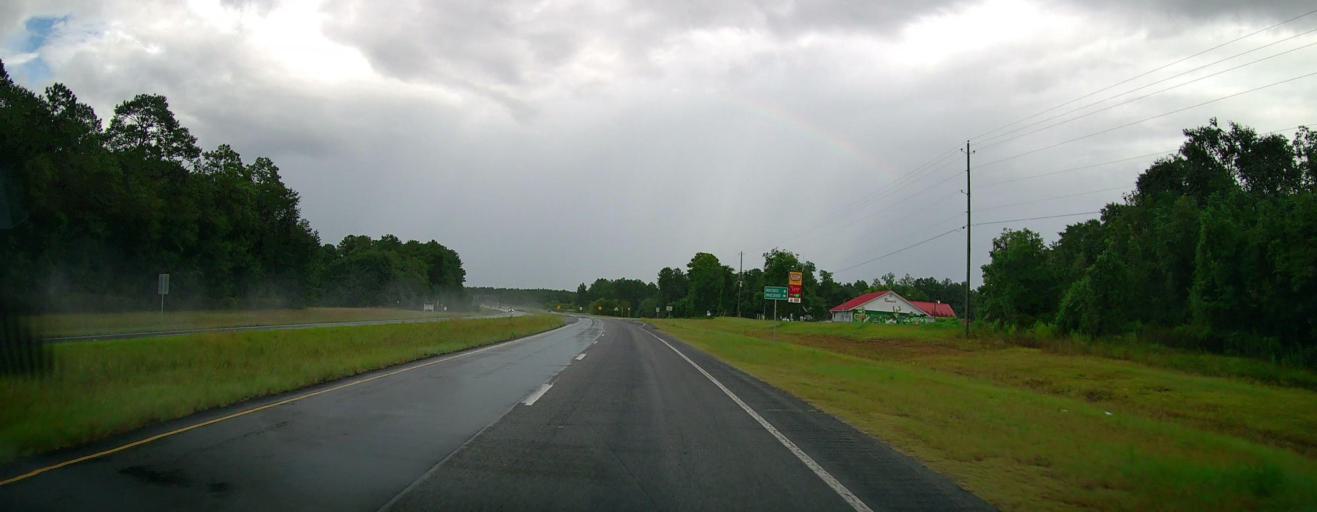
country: US
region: Georgia
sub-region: Ware County
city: Deenwood
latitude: 31.2543
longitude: -82.4804
